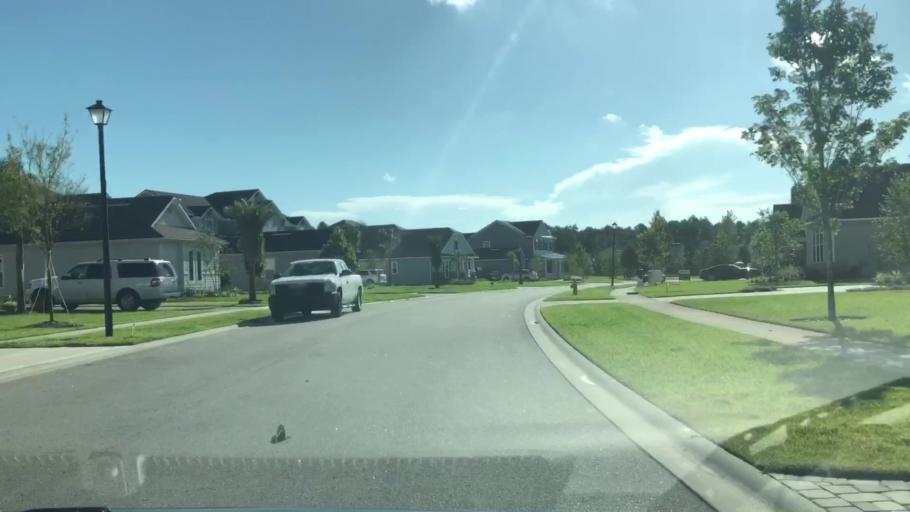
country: US
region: Florida
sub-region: Saint Johns County
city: Palm Valley
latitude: 30.1337
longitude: -81.4126
